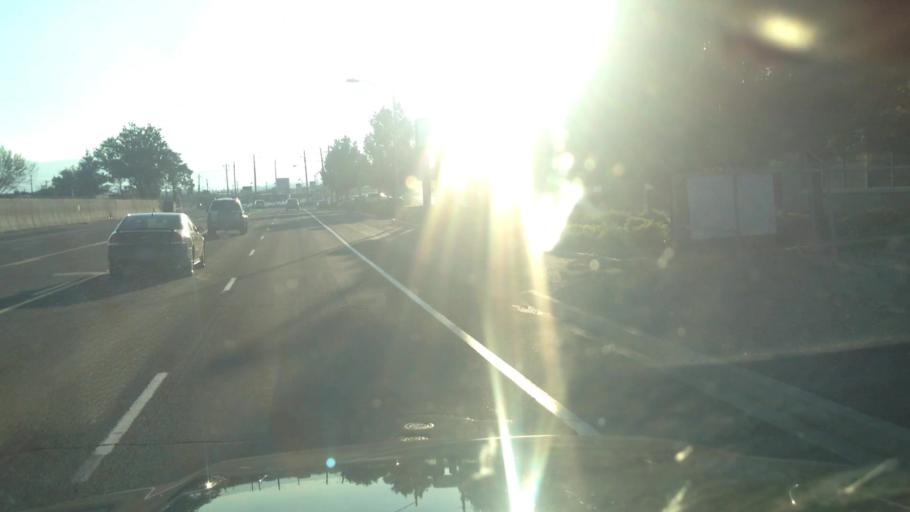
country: US
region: Nevada
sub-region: Washoe County
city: Sparks
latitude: 39.5174
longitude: -119.7698
